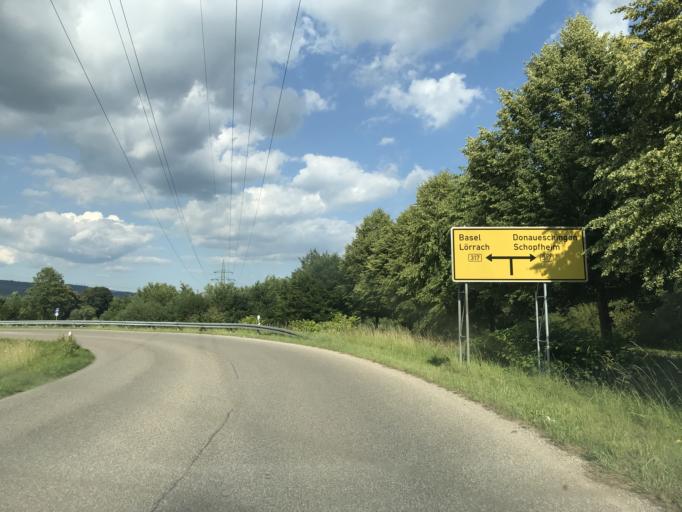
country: DE
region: Baden-Wuerttemberg
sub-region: Freiburg Region
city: Steinen
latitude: 47.6374
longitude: 7.7113
